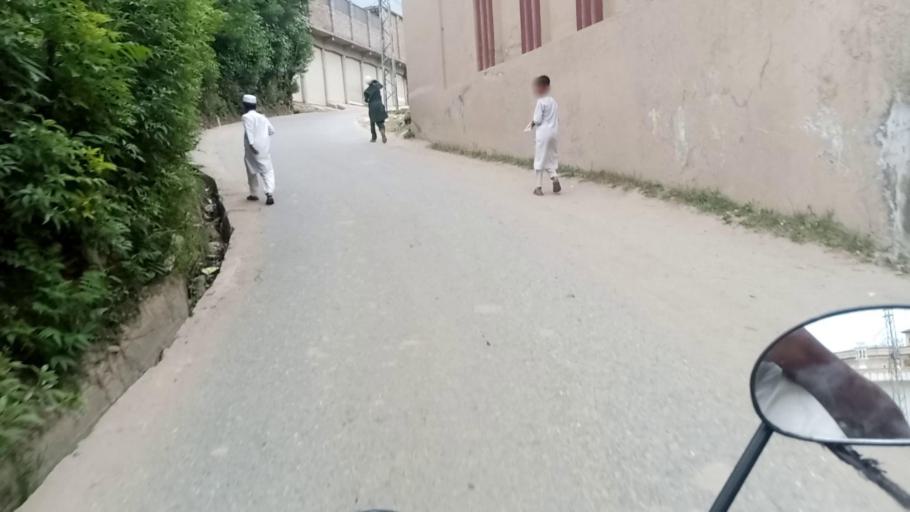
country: PK
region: Khyber Pakhtunkhwa
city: Mingora
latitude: 34.7577
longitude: 72.3787
